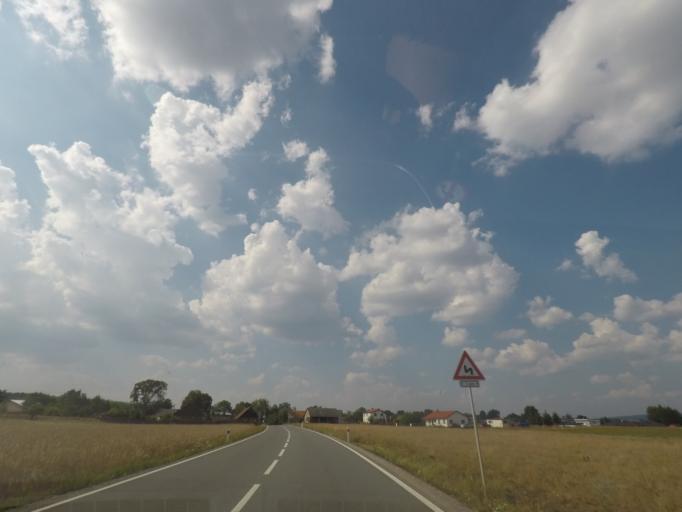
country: CZ
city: Albrechtice nad Orlici
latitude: 50.1152
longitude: 16.0725
